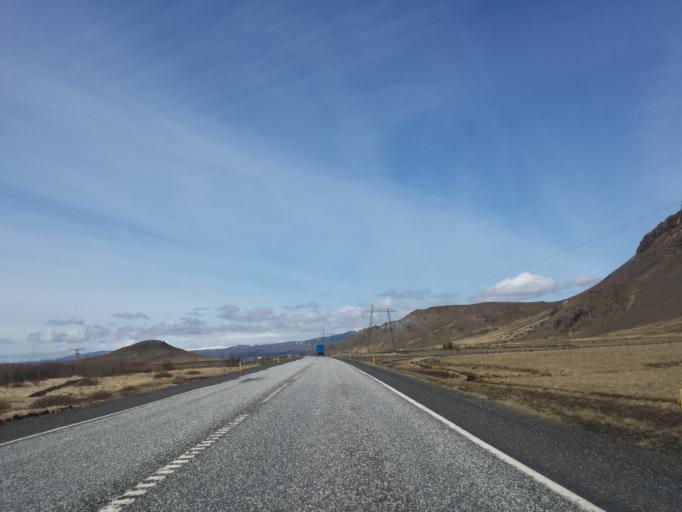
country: IS
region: South
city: Selfoss
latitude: 63.9562
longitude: -21.0542
